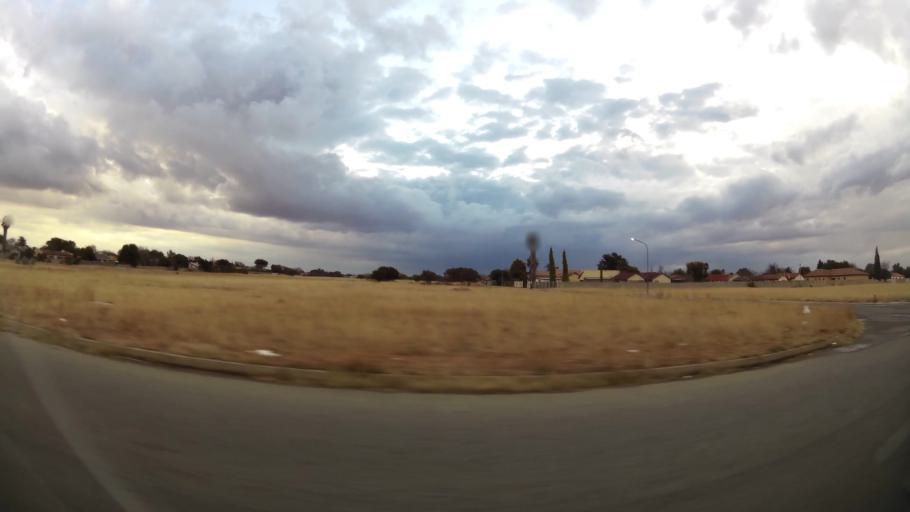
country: ZA
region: Orange Free State
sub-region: Lejweleputswa District Municipality
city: Welkom
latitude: -27.9455
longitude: 26.7348
